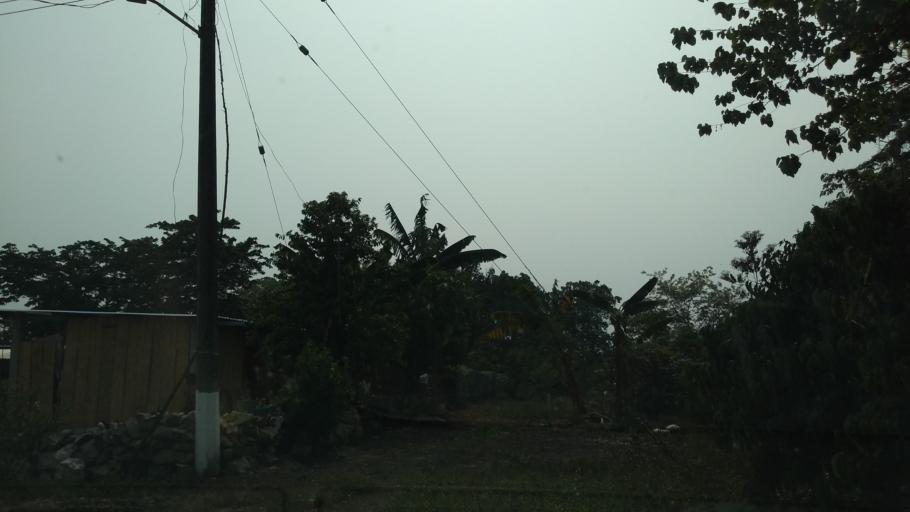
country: MX
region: Veracruz
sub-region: Tezonapa
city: Laguna Chica (Pueblo Nuevo)
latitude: 18.5442
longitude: -96.7614
